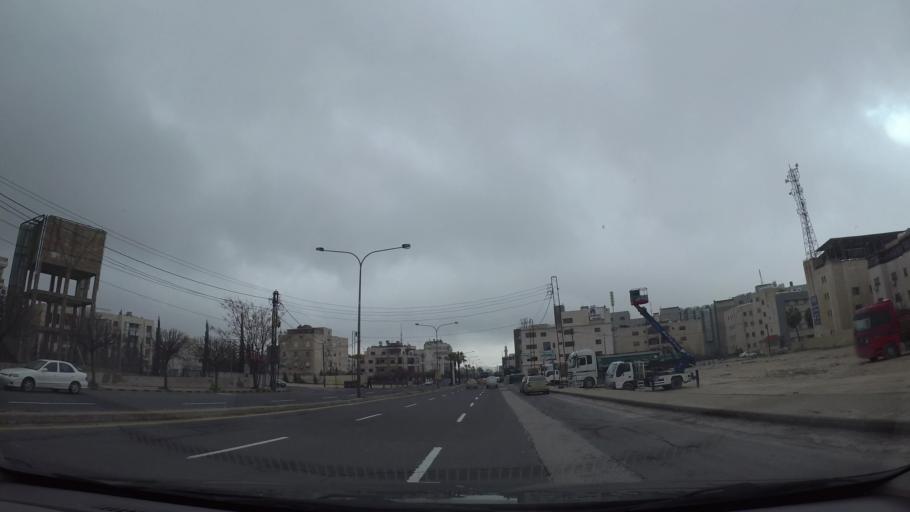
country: JO
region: Amman
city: Wadi as Sir
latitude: 31.9585
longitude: 35.8706
